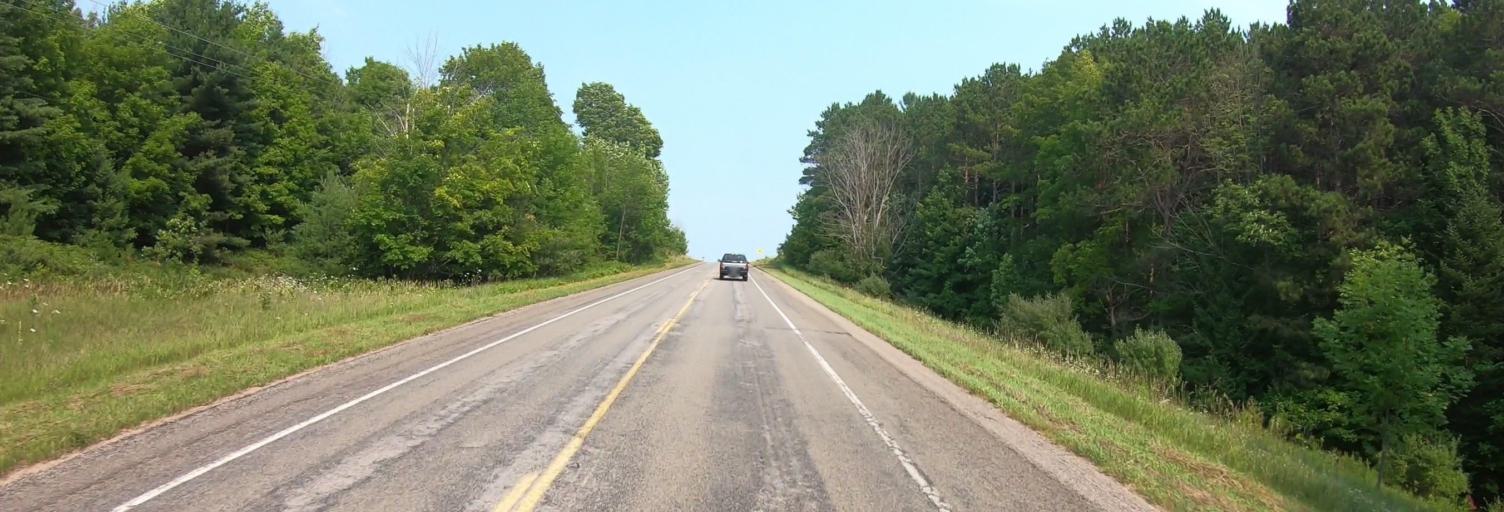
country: US
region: Michigan
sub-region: Charlevoix County
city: Charlevoix
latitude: 45.1851
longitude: -85.3084
